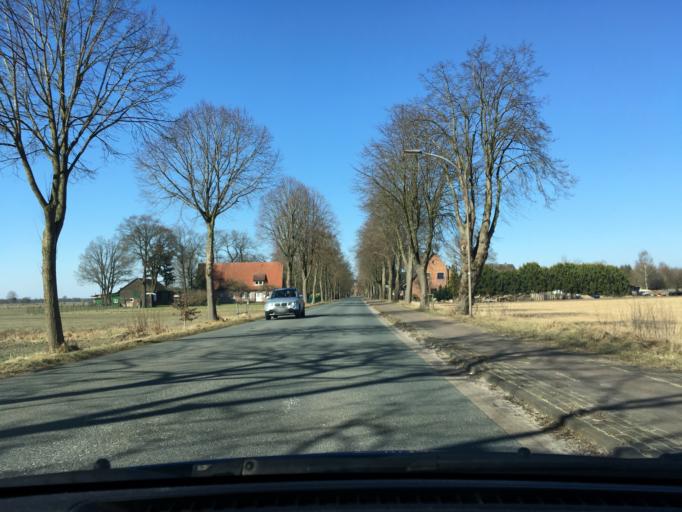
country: DE
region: Lower Saxony
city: Hemslingen
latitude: 53.0674
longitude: 9.6544
